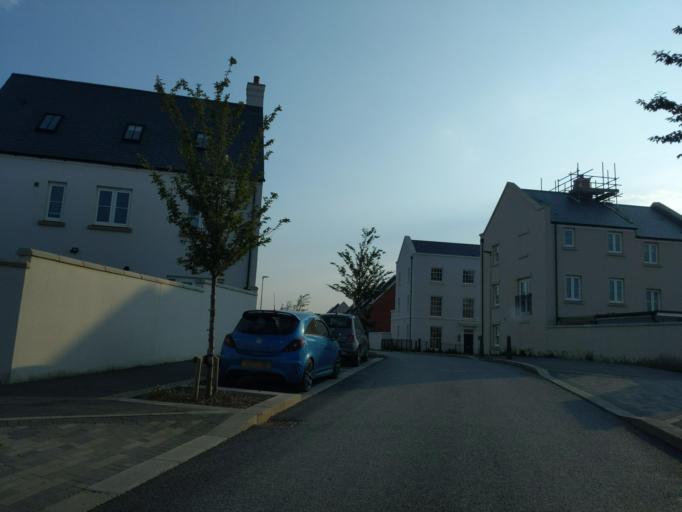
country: GB
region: England
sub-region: Devon
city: Plympton
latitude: 50.3640
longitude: -4.0485
